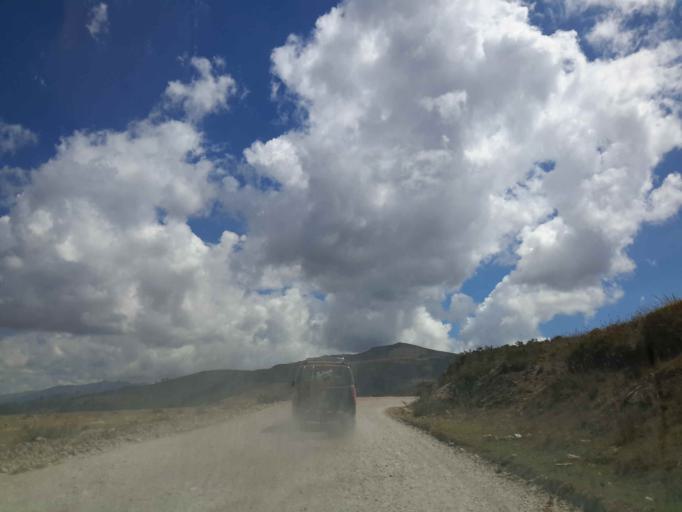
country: PE
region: Apurimac
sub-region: Provincia de Andahuaylas
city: San Jeronimo
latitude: -13.6414
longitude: -73.3335
